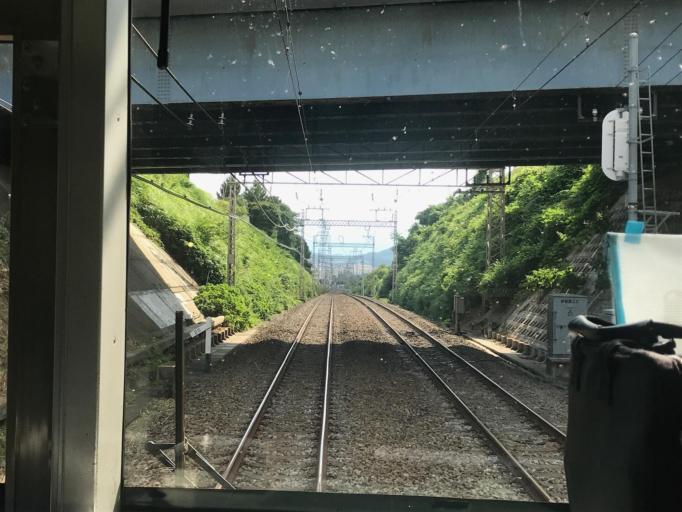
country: JP
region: Kanagawa
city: Isehara
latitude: 35.3917
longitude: 139.3047
